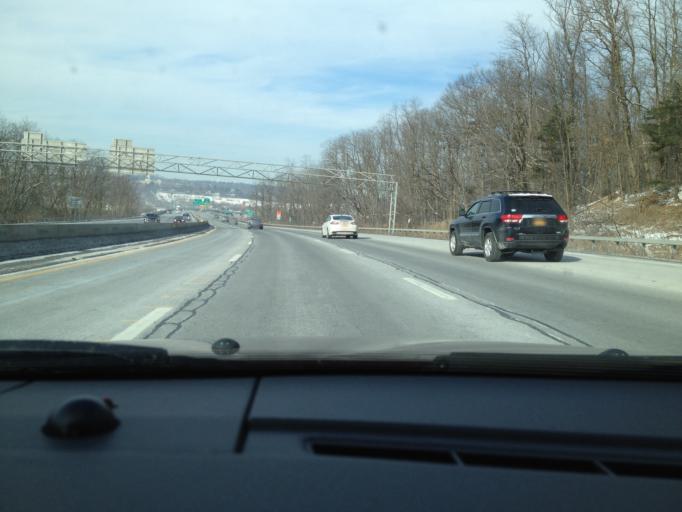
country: US
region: New York
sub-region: Rensselaer County
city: Rensselaer
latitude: 42.6619
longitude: -73.7234
